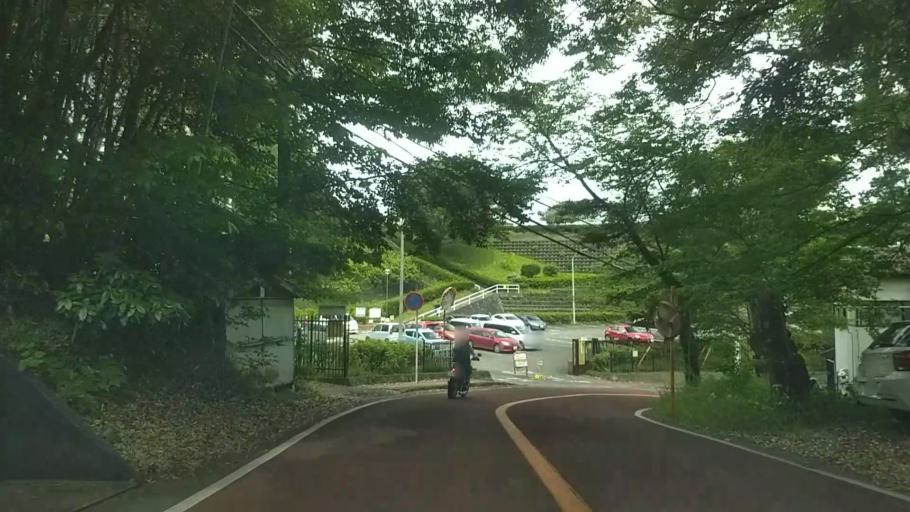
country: JP
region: Kanagawa
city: Kamakura
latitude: 35.3223
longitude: 139.5229
